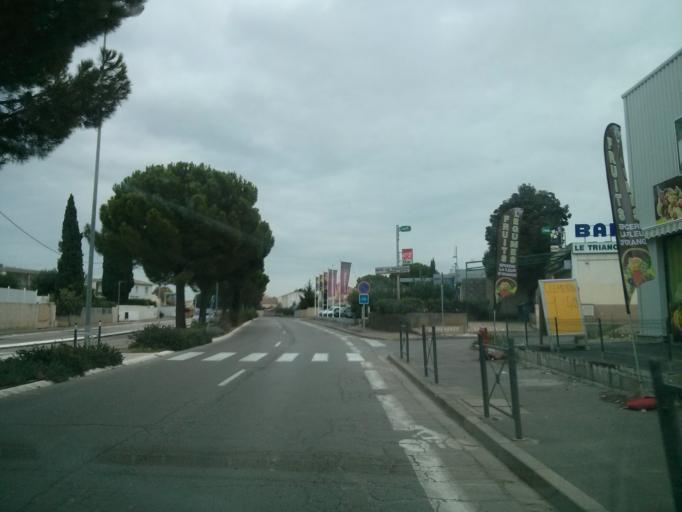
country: FR
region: Languedoc-Roussillon
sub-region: Departement de l'Herault
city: Lunel
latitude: 43.6725
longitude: 4.1414
